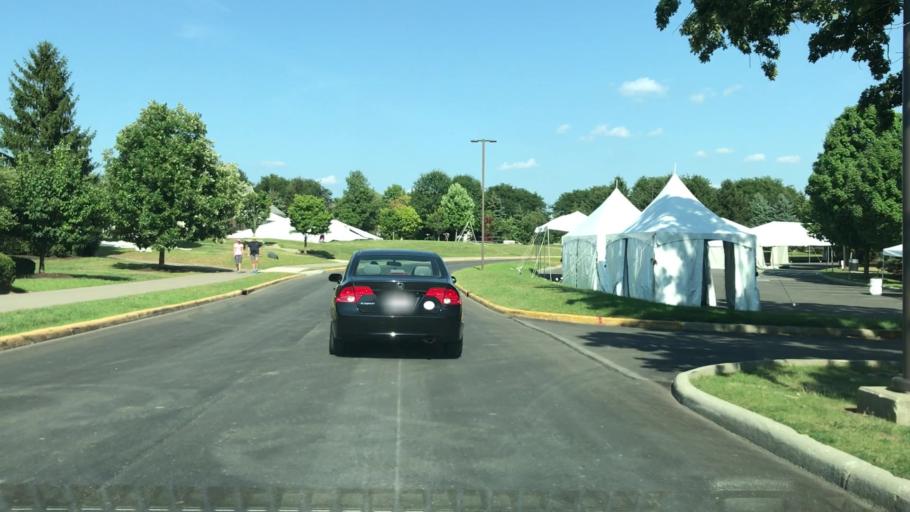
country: US
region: Ohio
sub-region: Franklin County
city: Dublin
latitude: 40.1061
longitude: -83.1380
